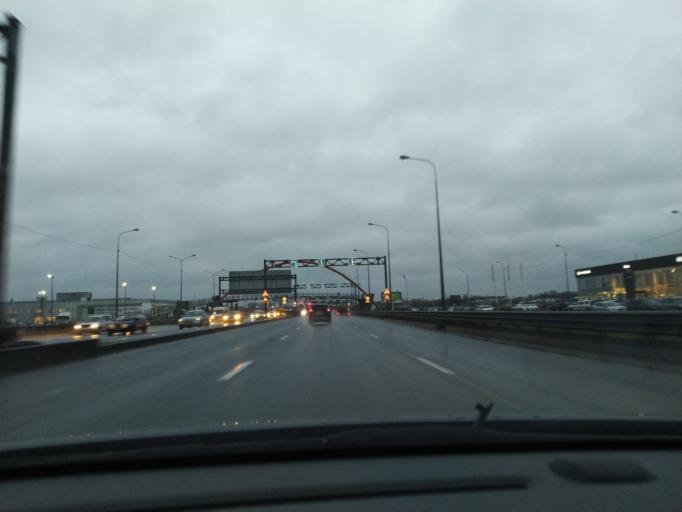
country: RU
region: St.-Petersburg
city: Sosnovaya Polyana
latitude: 59.8062
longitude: 30.1643
